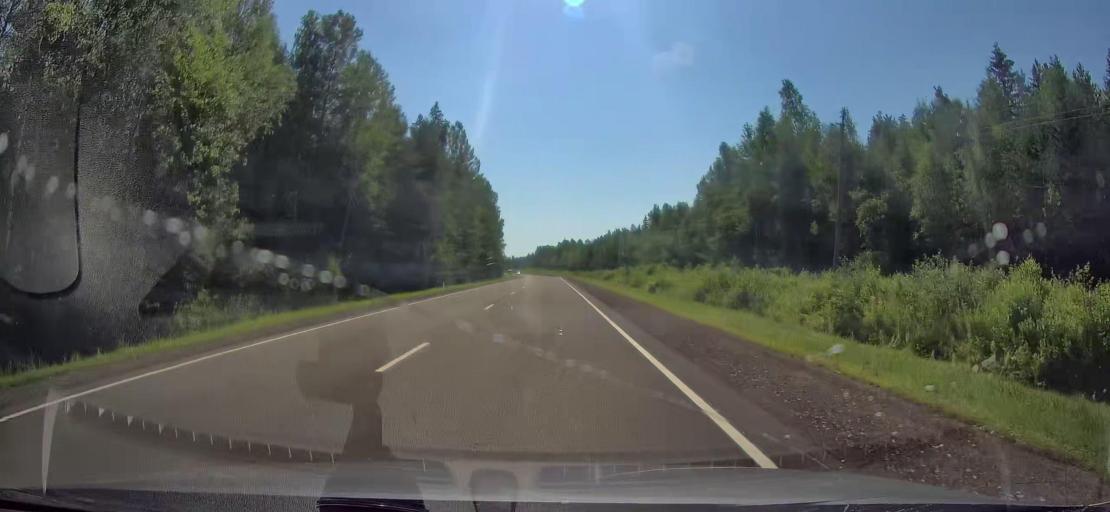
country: RU
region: Leningrad
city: Yefimovskiy
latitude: 59.3912
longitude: 34.7534
